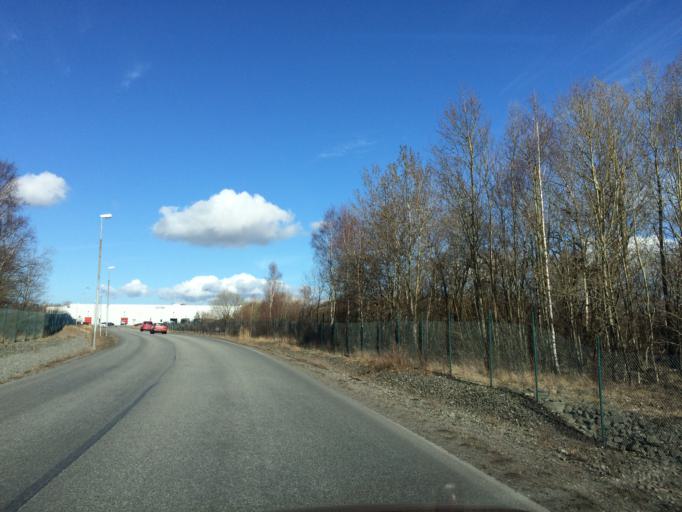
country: SE
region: Vaestra Goetaland
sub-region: Goteborg
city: Torslanda
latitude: 57.7113
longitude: 11.8167
